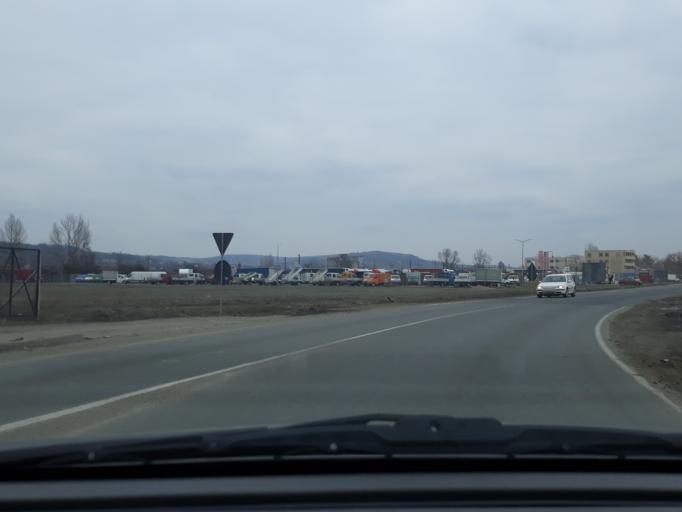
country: RO
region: Salaj
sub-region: Comuna Hereclean
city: Hereclean
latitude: 47.2244
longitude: 23.0214
